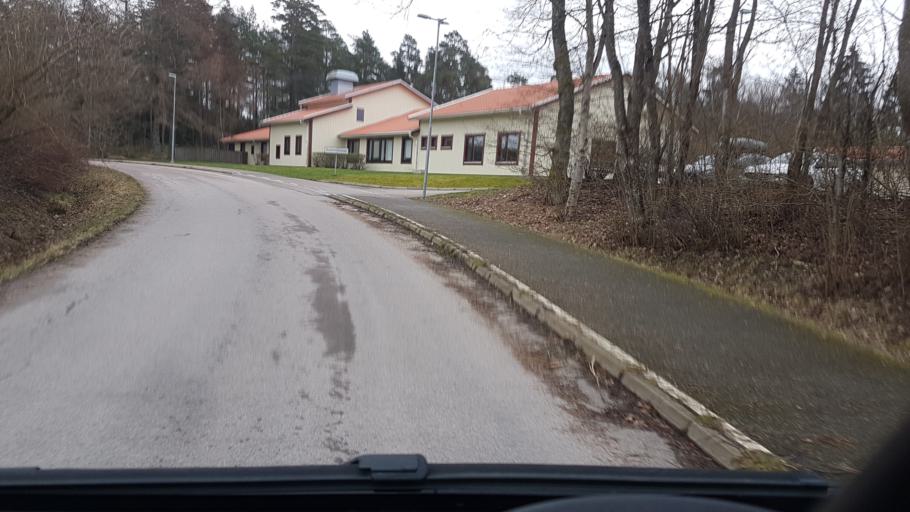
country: SE
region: Vaestra Goetaland
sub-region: Lerums Kommun
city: Stenkullen
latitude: 57.8073
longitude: 12.3391
